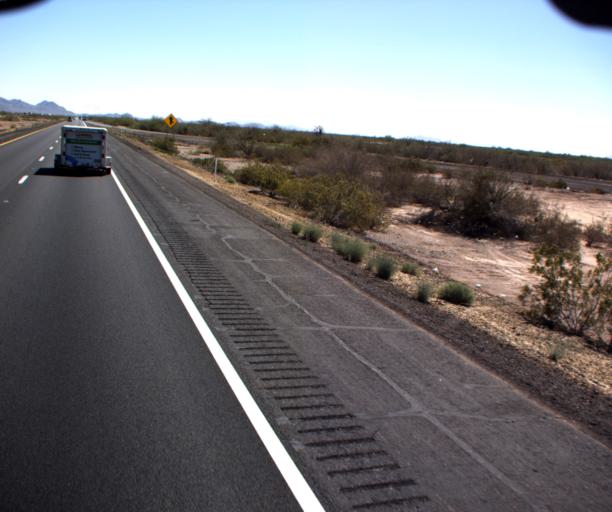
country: US
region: Arizona
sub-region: La Paz County
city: Salome
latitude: 33.6304
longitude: -113.7655
